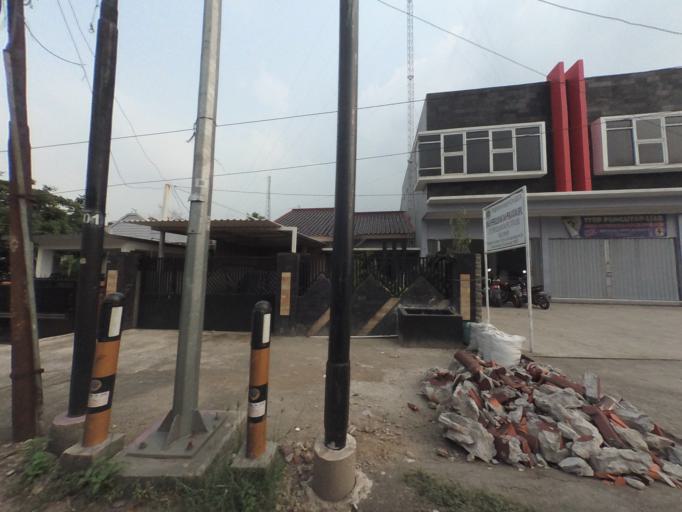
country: ID
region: West Java
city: Ciampea
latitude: -6.5672
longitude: 106.6716
